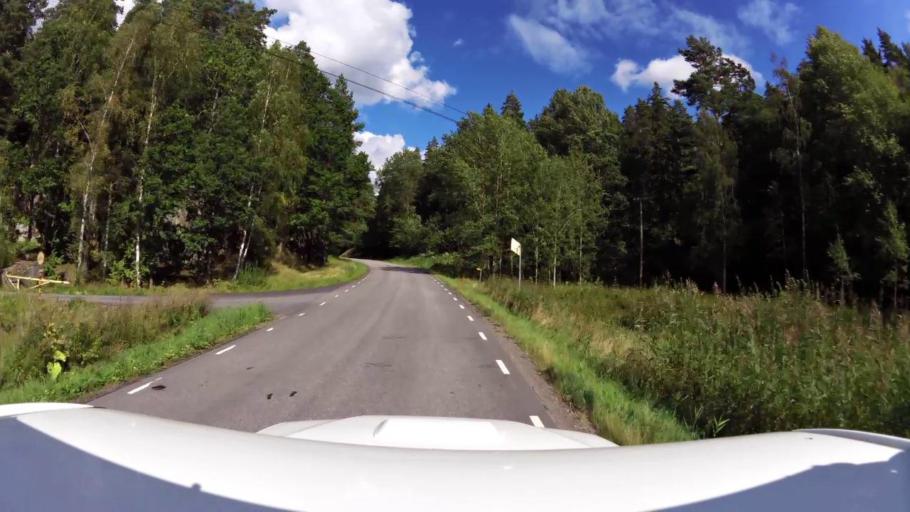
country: SE
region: OEstergoetland
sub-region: Kinda Kommun
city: Rimforsa
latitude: 58.2257
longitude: 15.7111
